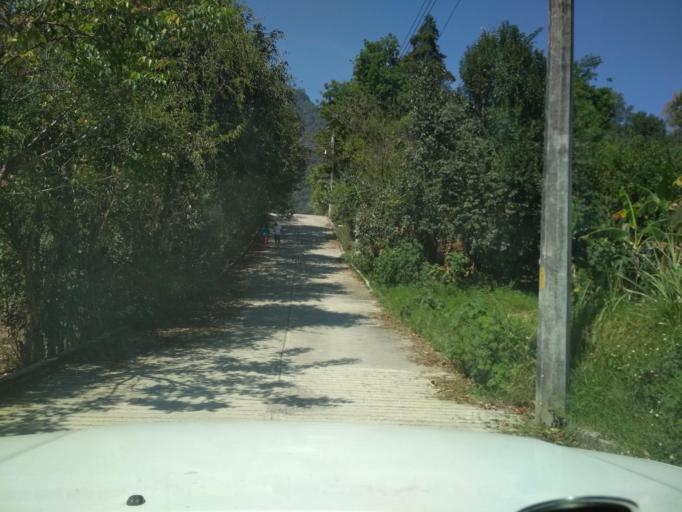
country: MX
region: Veracruz
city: Jalapilla
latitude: 18.8224
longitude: -97.0922
